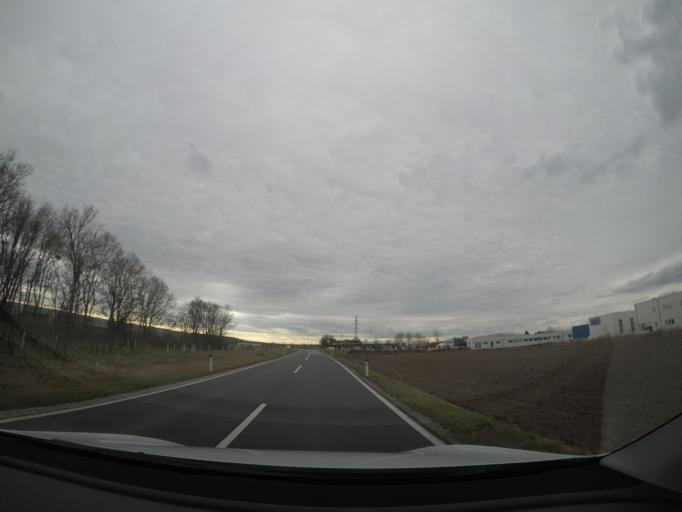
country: AT
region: Lower Austria
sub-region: Politischer Bezirk Modling
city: Biedermannsdorf
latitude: 48.0870
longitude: 16.3587
